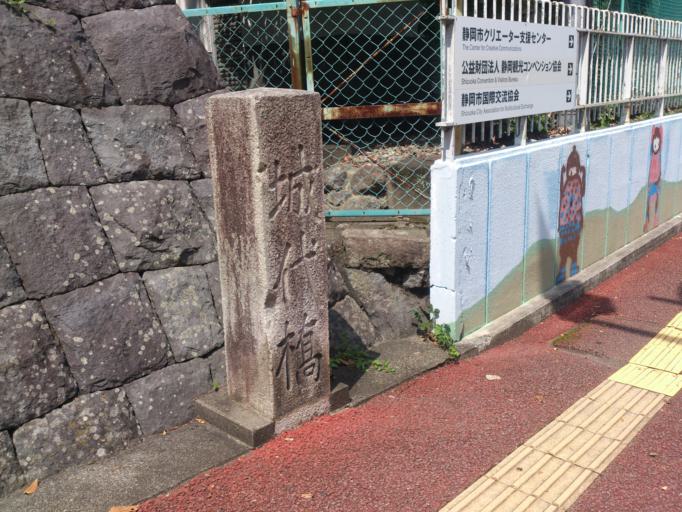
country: JP
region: Shizuoka
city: Shizuoka-shi
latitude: 34.9759
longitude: 138.3848
